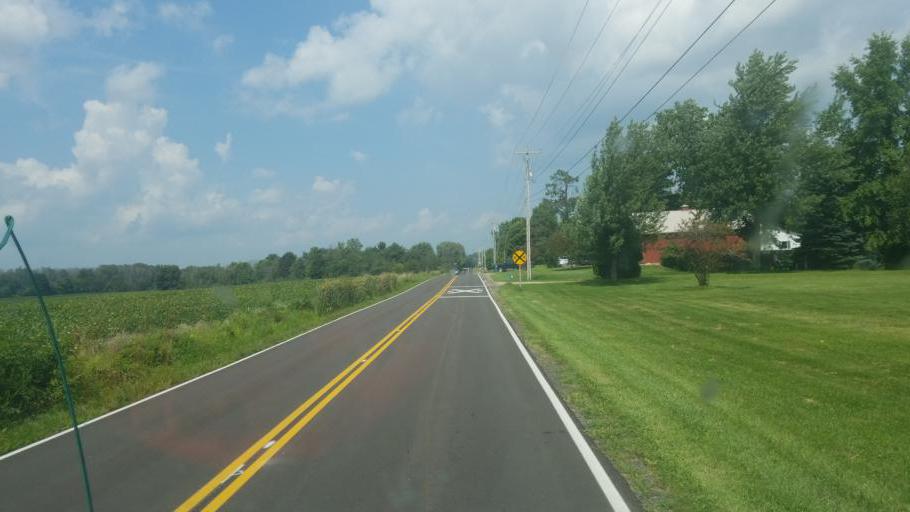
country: US
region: Ohio
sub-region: Richland County
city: Shelby
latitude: 40.8438
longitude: -82.6292
